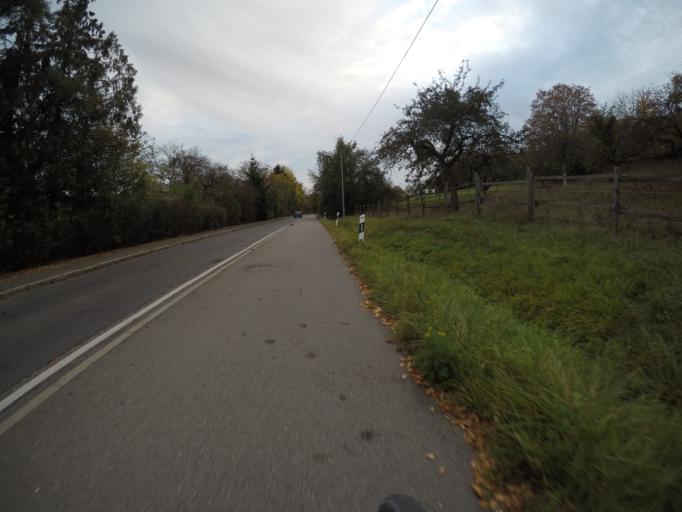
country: DE
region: Baden-Wuerttemberg
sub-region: Regierungsbezirk Stuttgart
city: Leinfelden-Echterdingen
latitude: 48.7368
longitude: 9.1255
